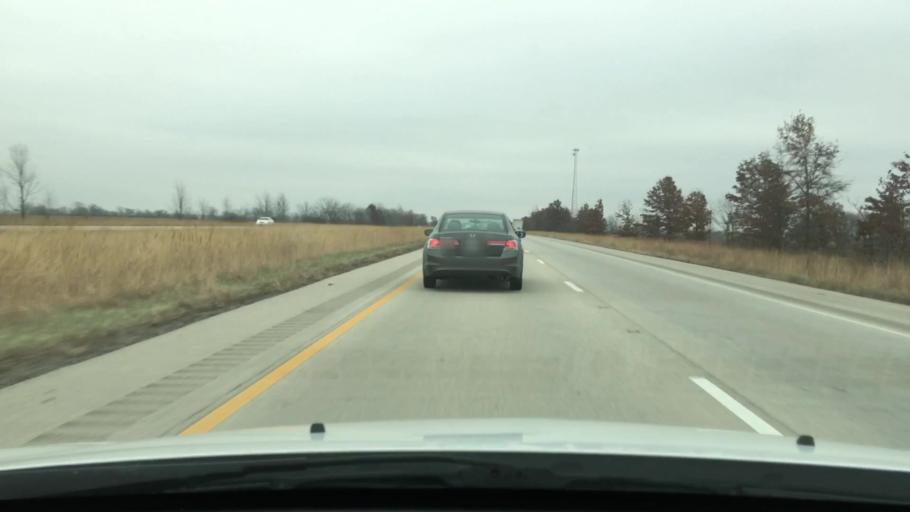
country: US
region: Illinois
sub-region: Sangamon County
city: New Berlin
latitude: 39.7405
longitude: -89.8793
